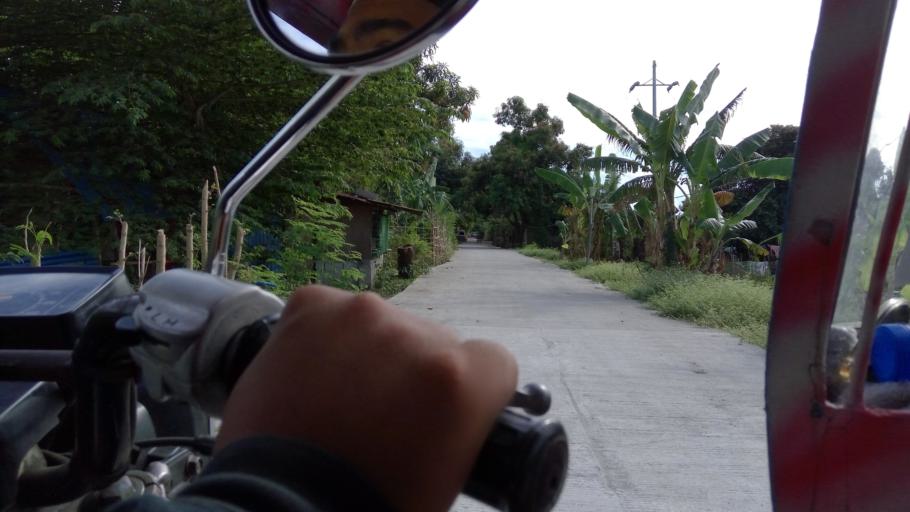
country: PH
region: Ilocos
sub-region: Province of La Union
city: San Eugenio
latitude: 16.3622
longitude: 120.3525
